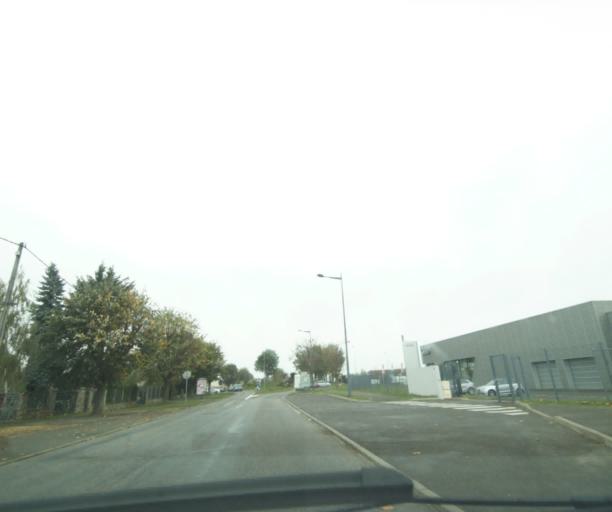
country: FR
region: Centre
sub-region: Departement d'Eure-et-Loir
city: Dreux
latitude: 48.7407
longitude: 1.3466
